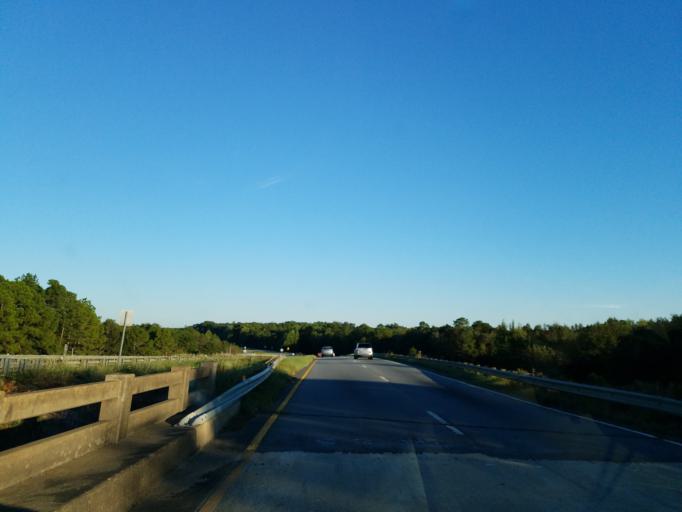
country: US
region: Georgia
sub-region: Worth County
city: Sylvester
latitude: 31.5127
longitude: -83.7771
